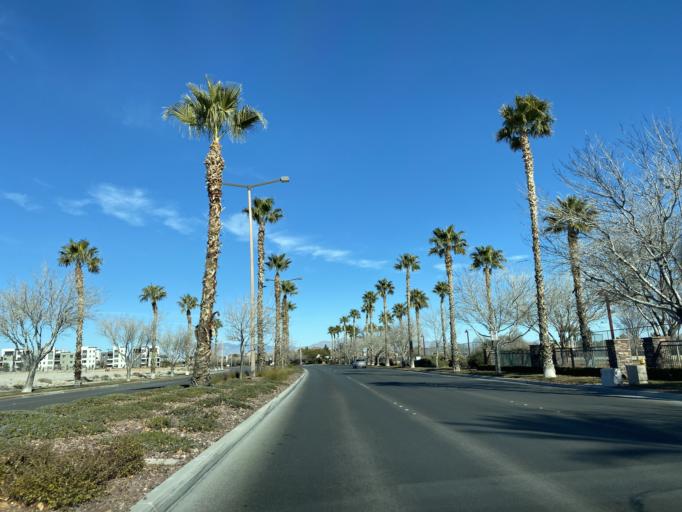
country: US
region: Nevada
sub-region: Clark County
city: Summerlin South
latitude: 36.1515
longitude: -115.3238
